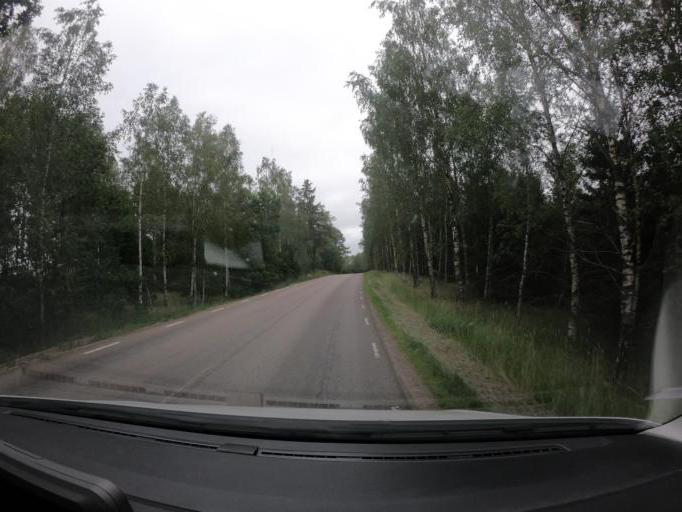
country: SE
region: Skane
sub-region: Perstorps Kommun
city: Perstorp
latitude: 56.0508
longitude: 13.3659
